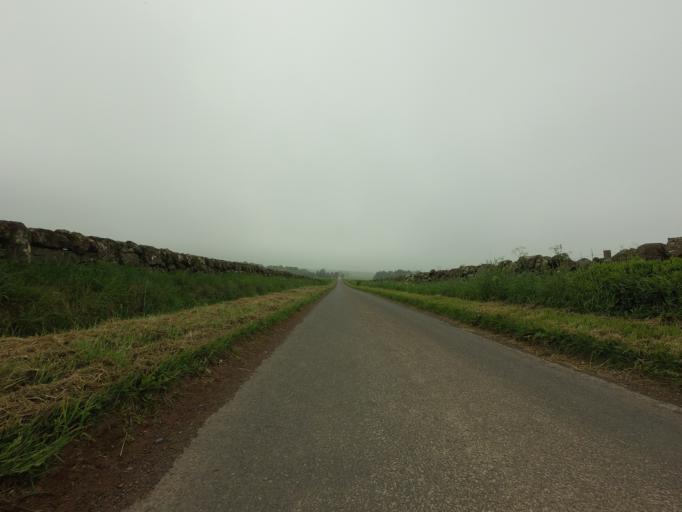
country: GB
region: Scotland
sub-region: Perth and Kinross
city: Abernethy
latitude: 56.2551
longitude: -3.3245
